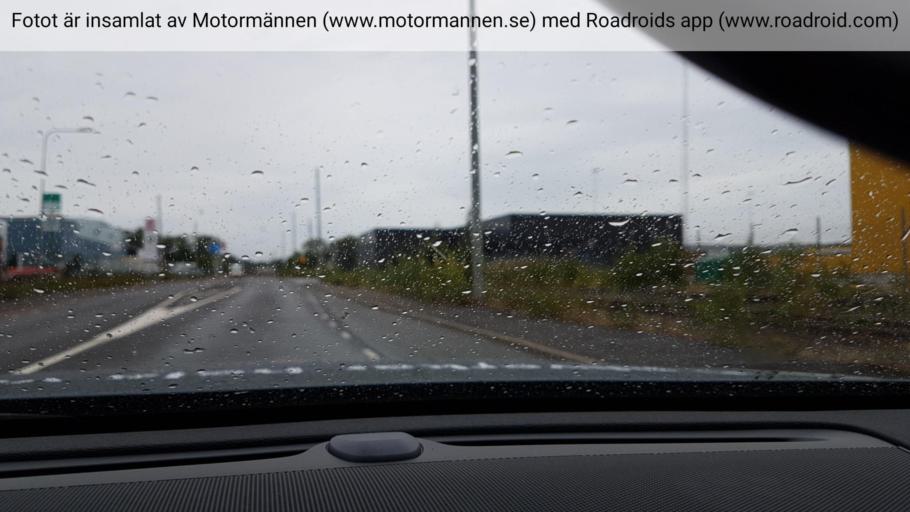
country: SE
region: Vaestra Goetaland
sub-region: Goteborg
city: Hammarkullen
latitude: 57.7536
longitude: 11.9958
